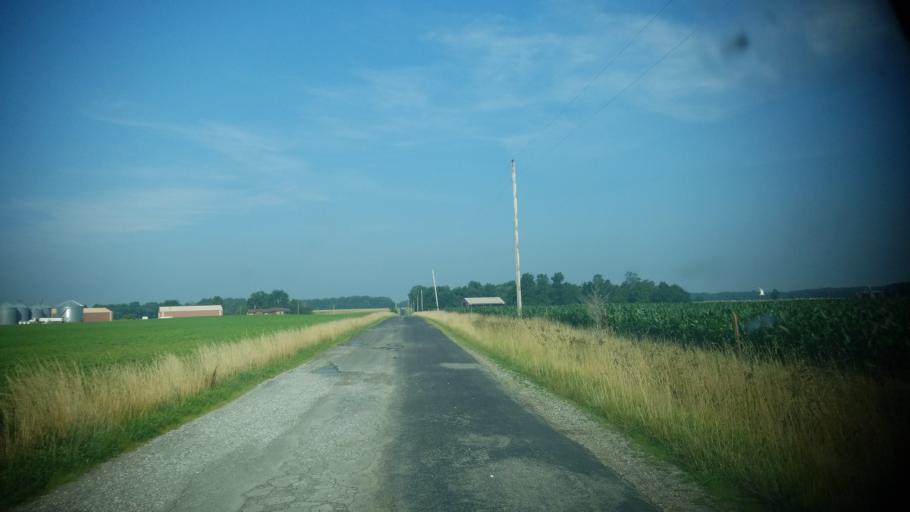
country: US
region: Illinois
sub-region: Clay County
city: Flora
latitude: 38.6024
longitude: -88.3833
